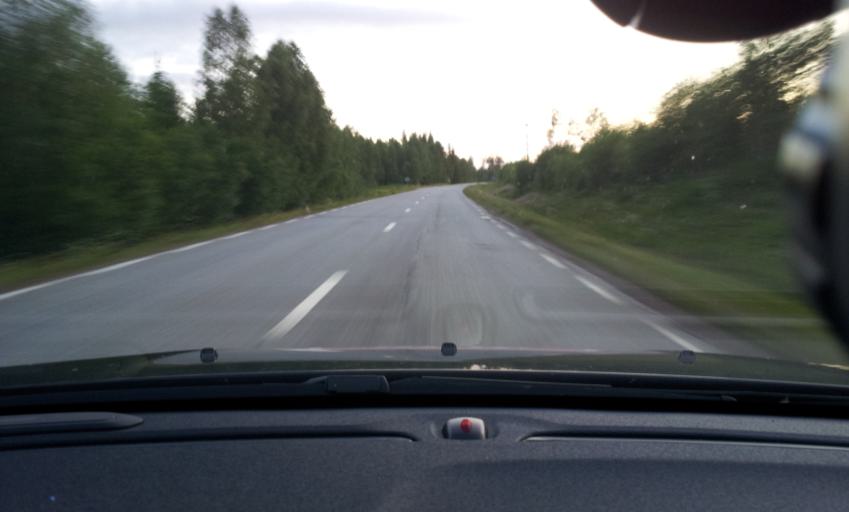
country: SE
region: Jaemtland
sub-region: Ragunda Kommun
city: Hammarstrand
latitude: 63.0184
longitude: 16.1855
